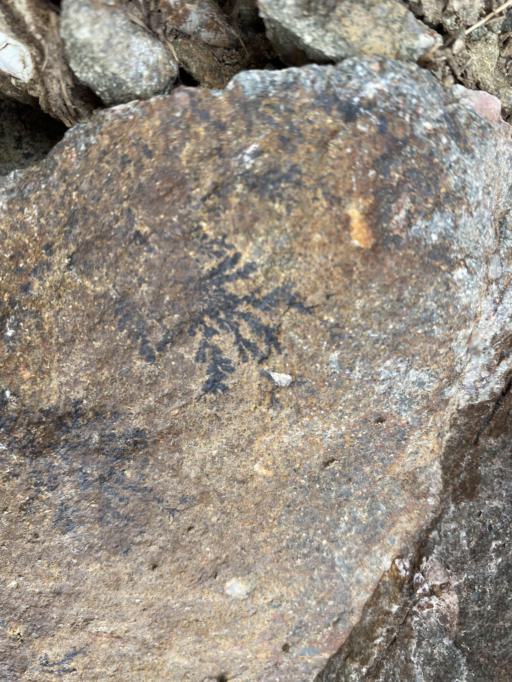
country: KZ
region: Ongtustik Qazaqstan
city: Kentau
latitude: 43.8398
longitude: 68.4986
